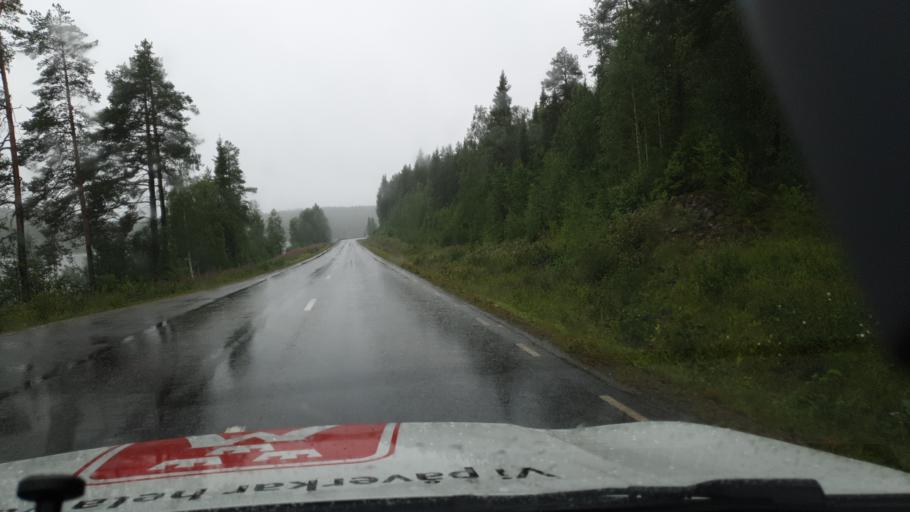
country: SE
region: Vaesterbotten
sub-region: Norsjo Kommun
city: Norsjoe
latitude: 64.8557
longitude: 19.7394
